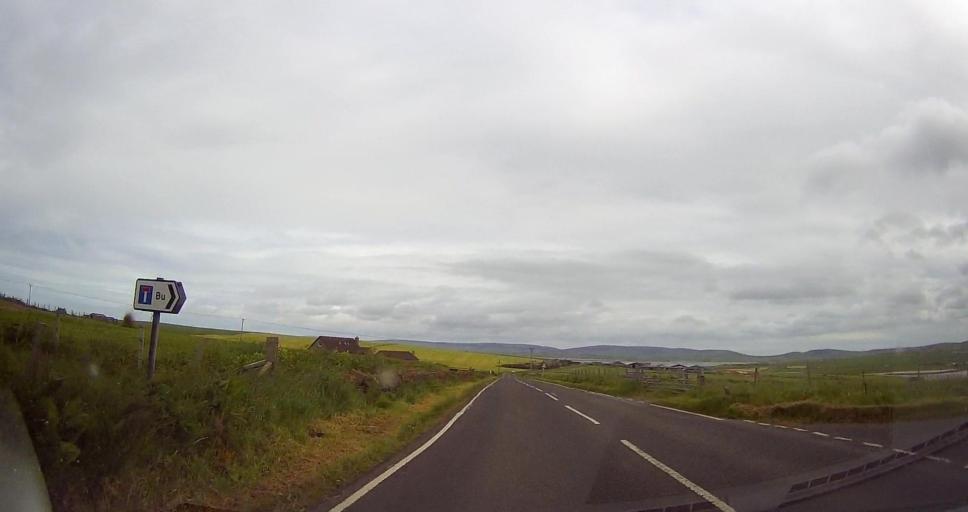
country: GB
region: Scotland
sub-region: Orkney Islands
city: Stromness
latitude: 58.9753
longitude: -3.2760
